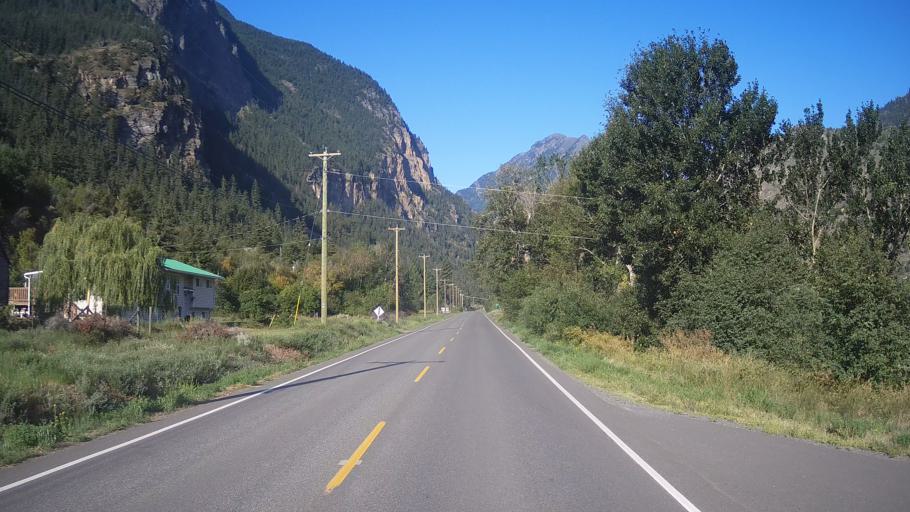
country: CA
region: British Columbia
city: Lillooet
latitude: 50.6723
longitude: -121.9414
